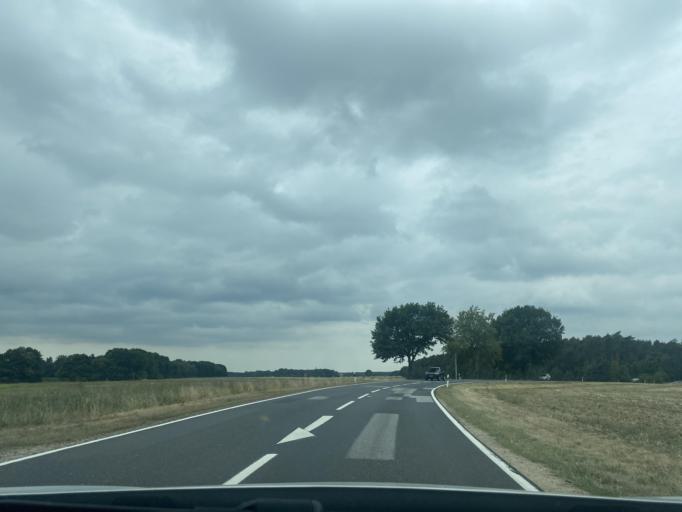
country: DE
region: Saxony
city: Mucka
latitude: 51.2828
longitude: 14.6657
